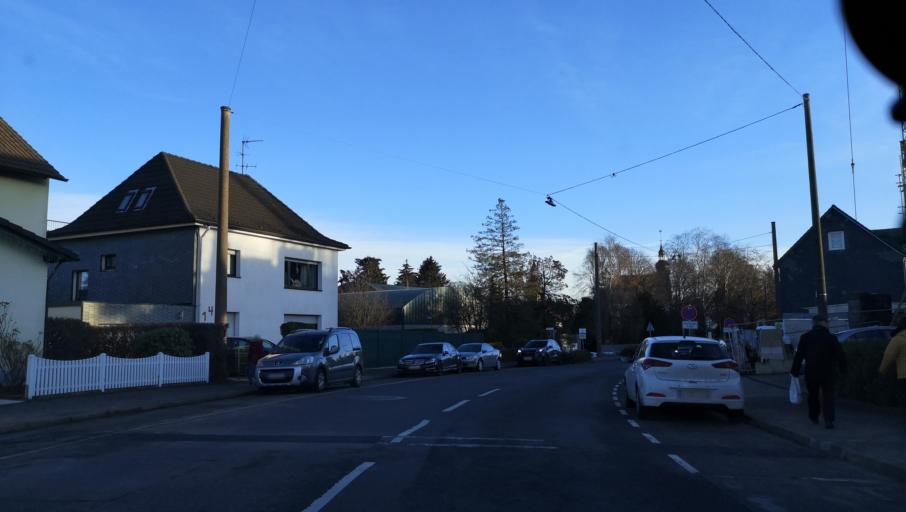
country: DE
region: North Rhine-Westphalia
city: Radevormwald
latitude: 51.2053
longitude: 7.3537
